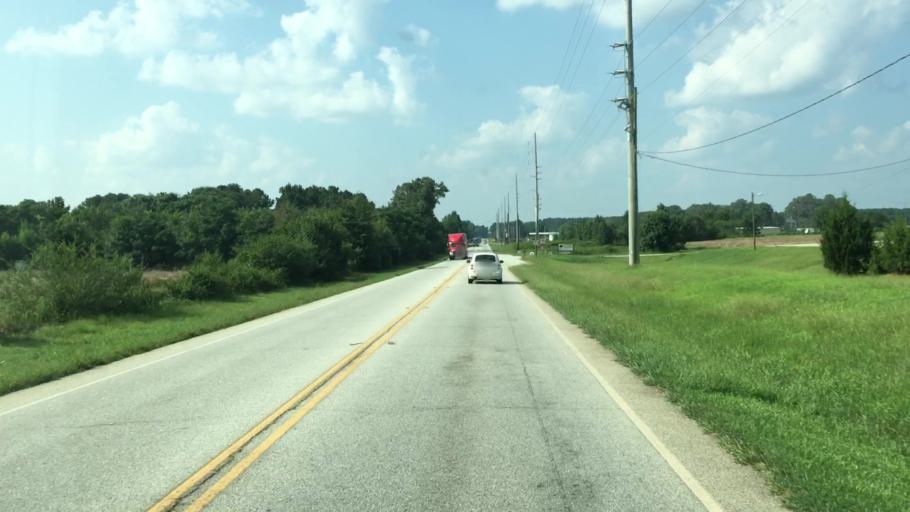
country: US
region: Georgia
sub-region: Walton County
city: Social Circle
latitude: 33.5944
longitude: -83.7491
